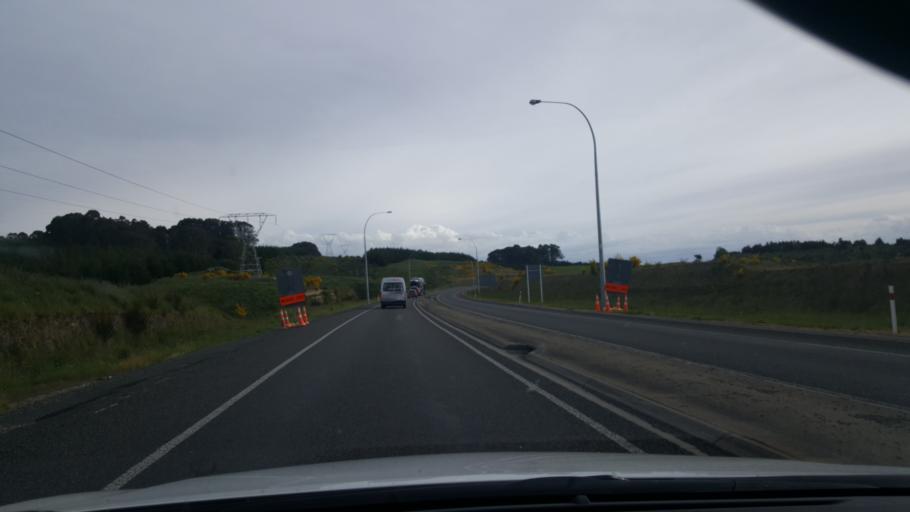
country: NZ
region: Waikato
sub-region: Taupo District
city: Taupo
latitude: -38.7053
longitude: 176.1121
